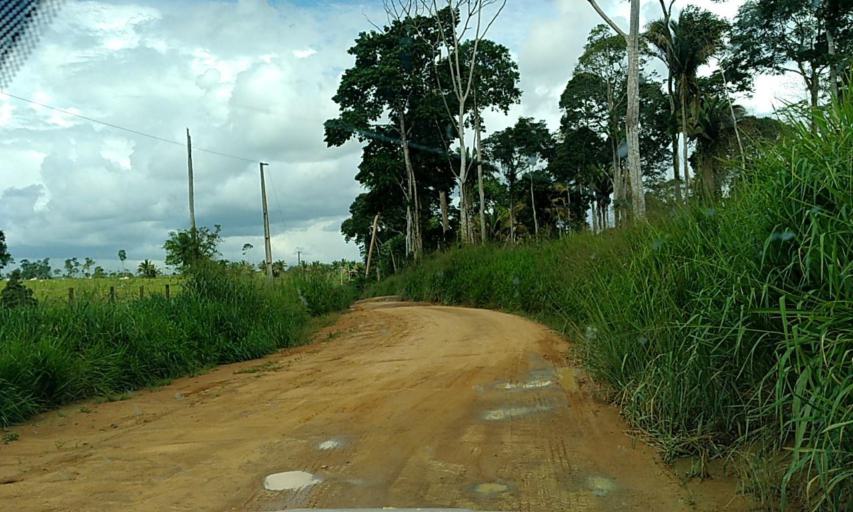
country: BR
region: Para
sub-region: Altamira
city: Altamira
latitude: -3.2335
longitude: -52.7343
